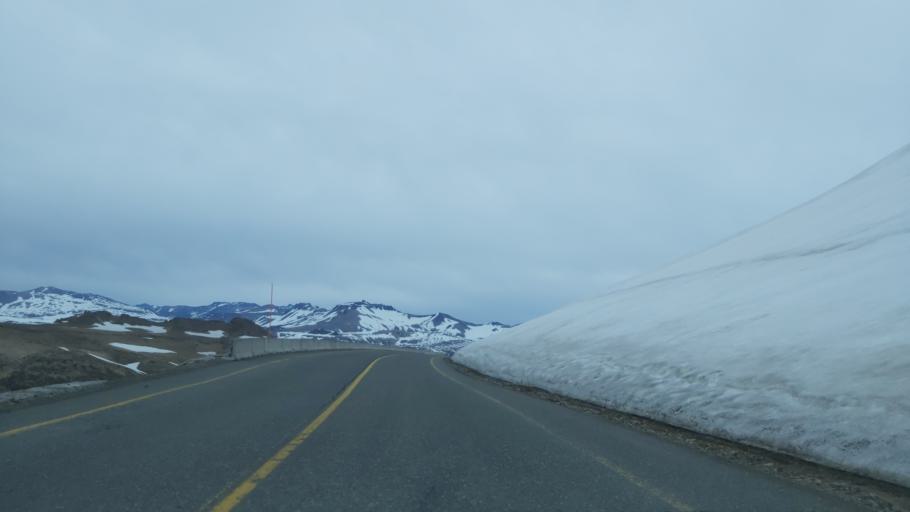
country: CL
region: Maule
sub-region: Provincia de Linares
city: Colbun
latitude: -36.0178
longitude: -70.4984
